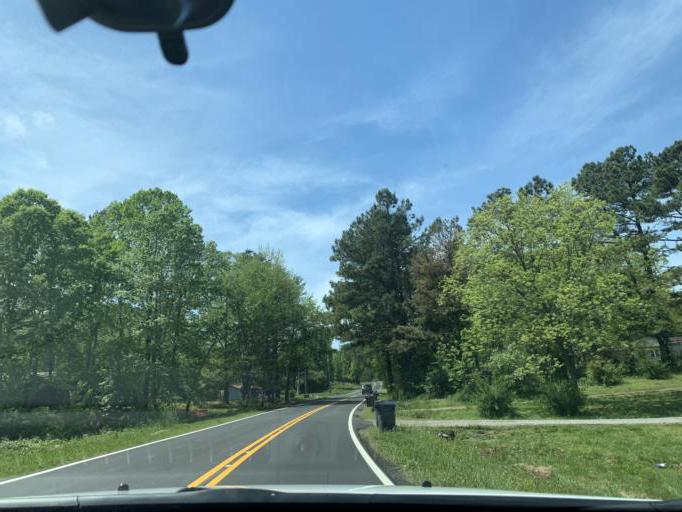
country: US
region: Georgia
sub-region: Forsyth County
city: Cumming
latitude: 34.2632
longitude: -84.0407
